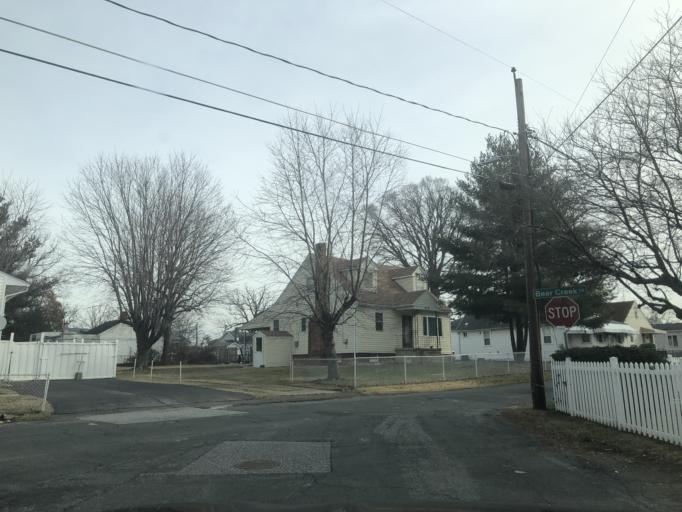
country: US
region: Maryland
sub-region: Baltimore County
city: Dundalk
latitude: 39.2655
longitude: -76.4823
